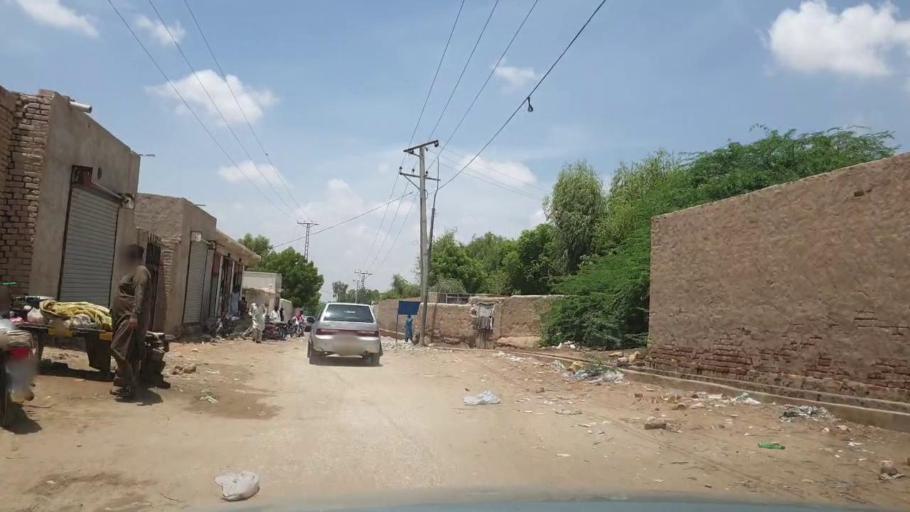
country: PK
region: Sindh
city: Kot Diji
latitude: 27.1603
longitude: 68.9649
